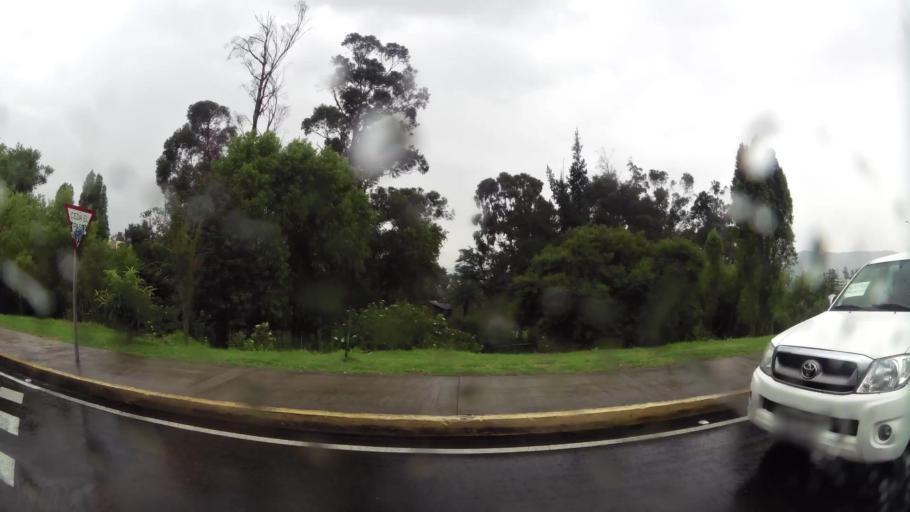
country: EC
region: Pichincha
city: Sangolqui
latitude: -0.3184
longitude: -78.4483
